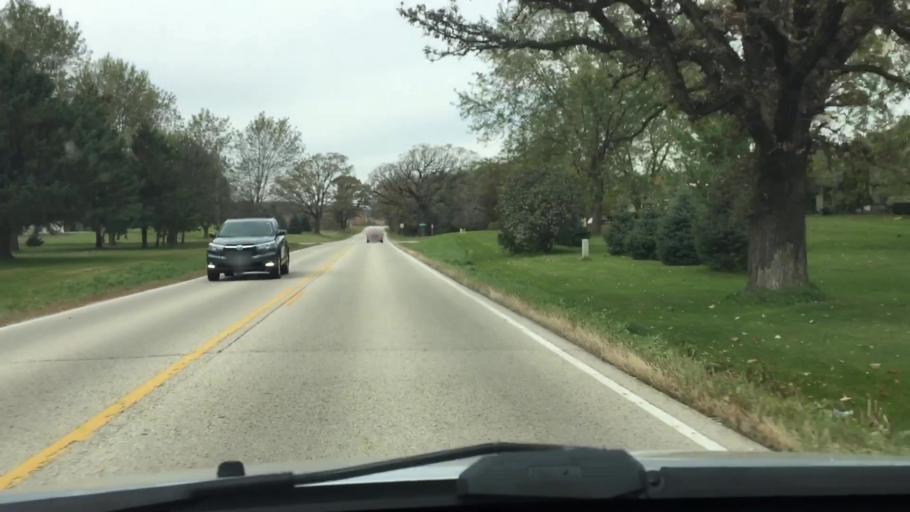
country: US
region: Wisconsin
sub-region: Waukesha County
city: Mukwonago
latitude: 42.8831
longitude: -88.3693
